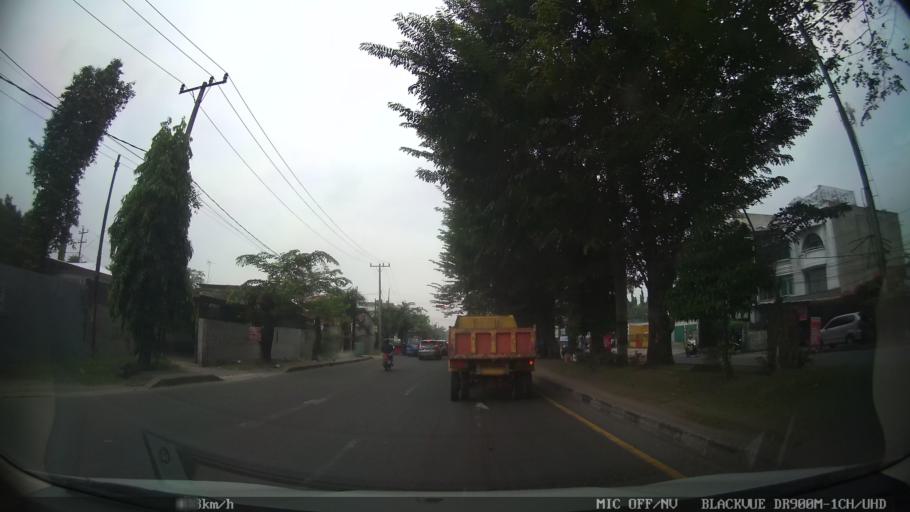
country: ID
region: North Sumatra
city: Deli Tua
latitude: 3.5381
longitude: 98.6905
